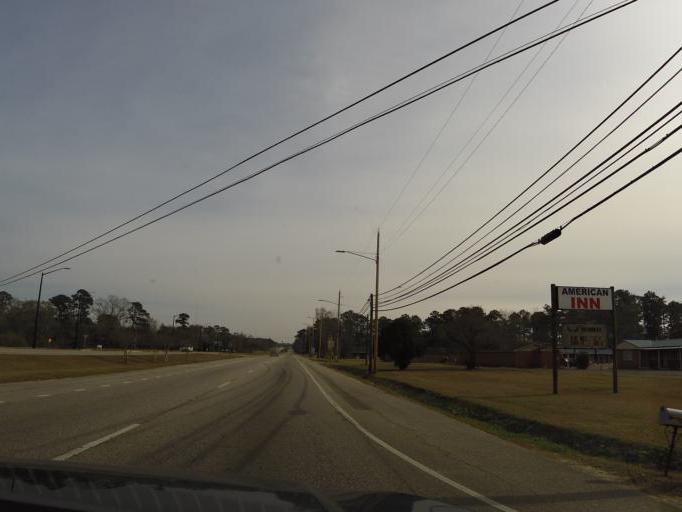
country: US
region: Alabama
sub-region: Houston County
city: Cowarts
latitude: 31.2046
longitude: -85.3485
